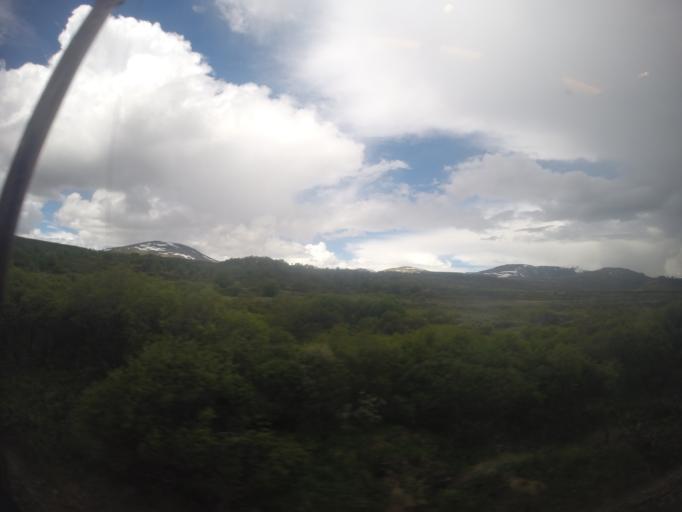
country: NO
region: Sor-Trondelag
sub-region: Oppdal
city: Oppdal
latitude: 62.2737
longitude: 9.5813
